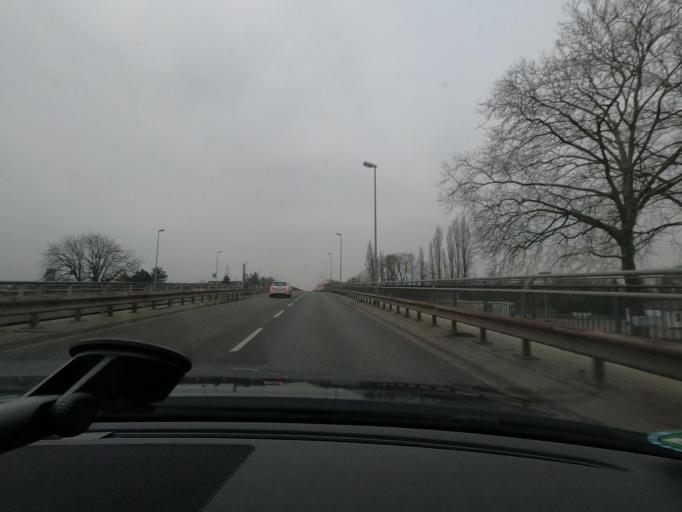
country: DE
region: North Rhine-Westphalia
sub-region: Regierungsbezirk Dusseldorf
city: Willich
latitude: 51.3064
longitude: 6.5439
